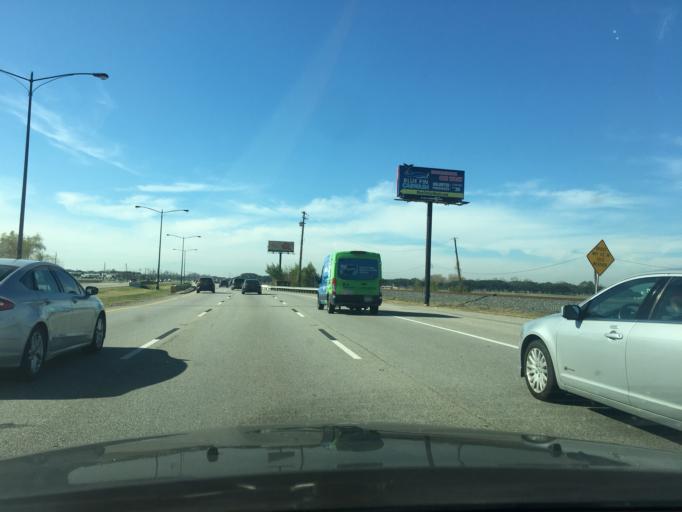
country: US
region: Texas
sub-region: Fort Bend County
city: Sugar Land
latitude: 29.6127
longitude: -95.6514
